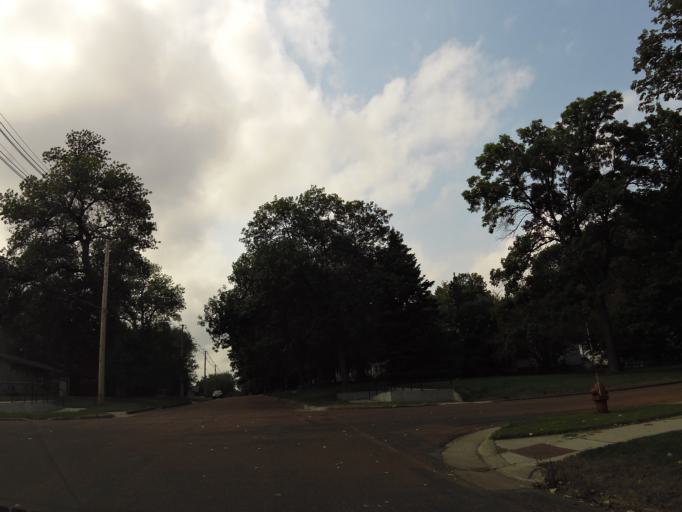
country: US
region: South Dakota
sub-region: Codington County
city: Watertown
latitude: 44.9059
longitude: -97.1142
